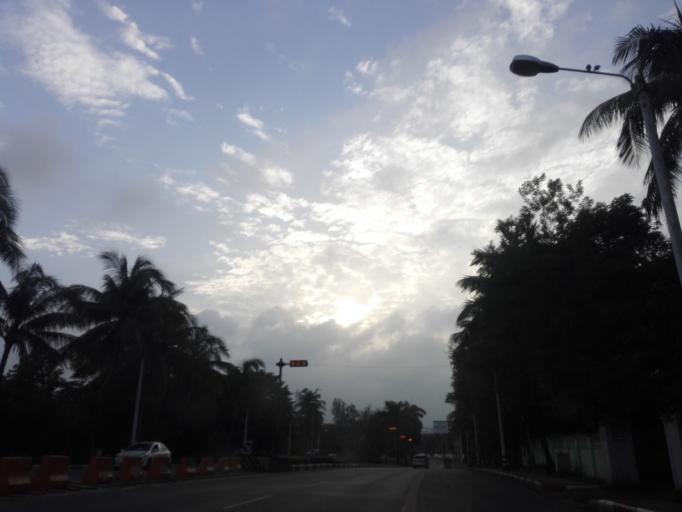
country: MM
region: Yangon
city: Yangon
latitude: 16.8491
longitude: 96.1377
